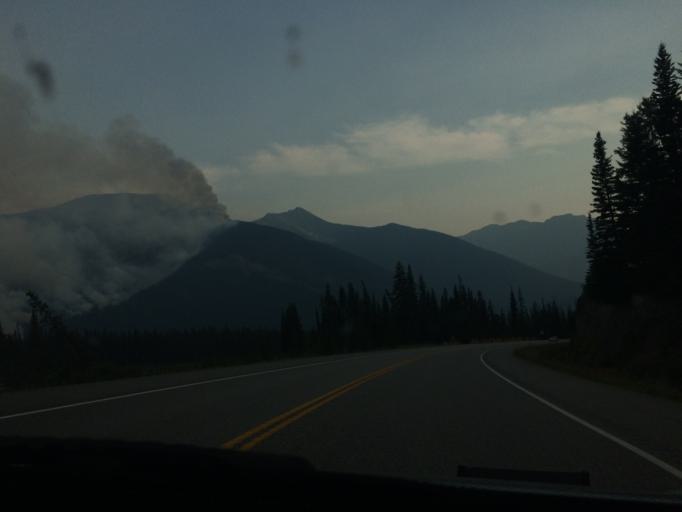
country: CA
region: Alberta
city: Banff
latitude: 50.9739
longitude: -115.9471
